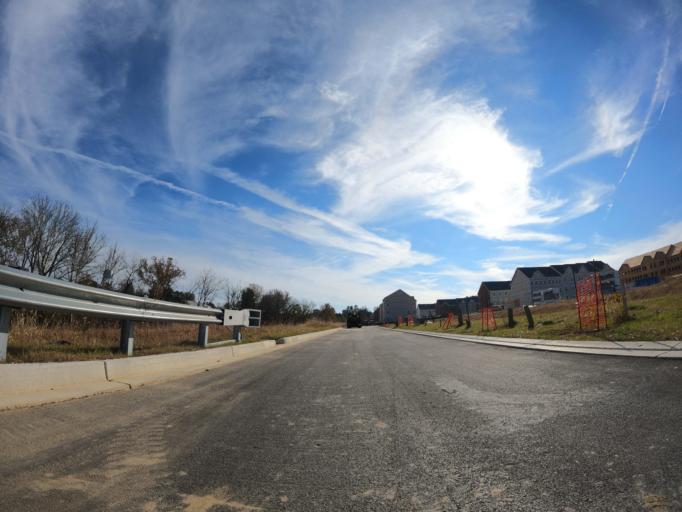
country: US
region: Maryland
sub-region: Carroll County
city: Sykesville
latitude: 39.3800
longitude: -76.9637
